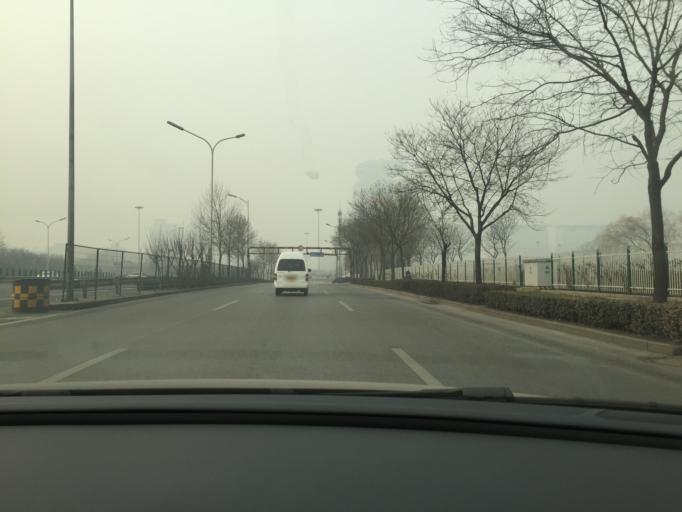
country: CN
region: Beijing
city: Datun
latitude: 39.9871
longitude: 116.3917
